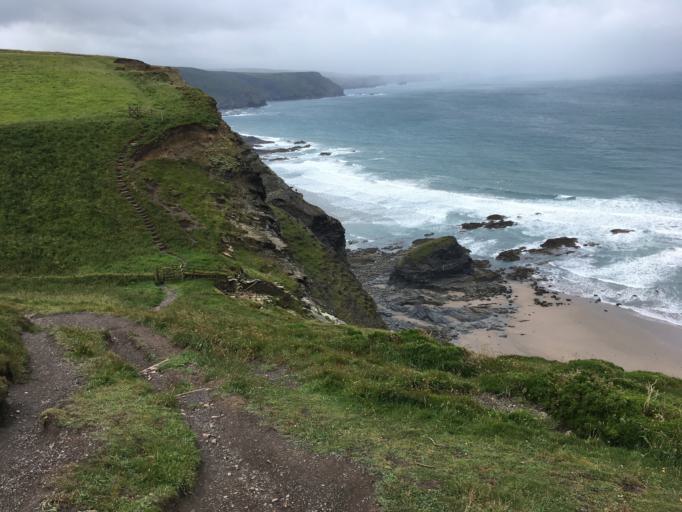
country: GB
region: England
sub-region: Cornwall
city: Jacobstow
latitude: 50.7325
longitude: -4.6481
